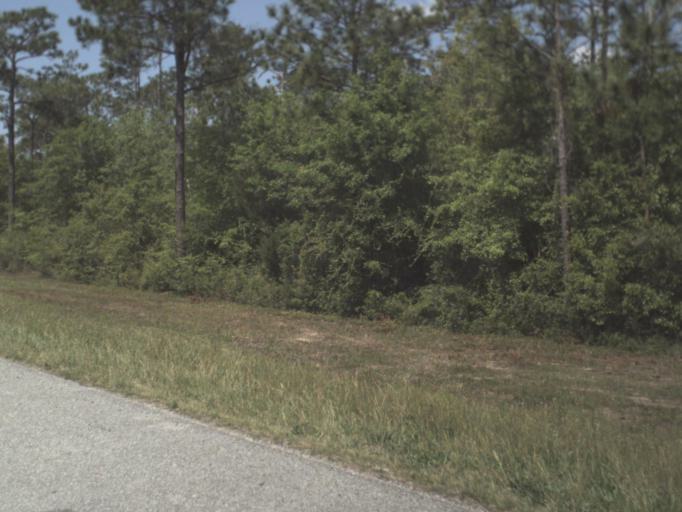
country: US
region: Florida
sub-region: Santa Rosa County
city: Bagdad
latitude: 30.5619
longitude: -87.0421
